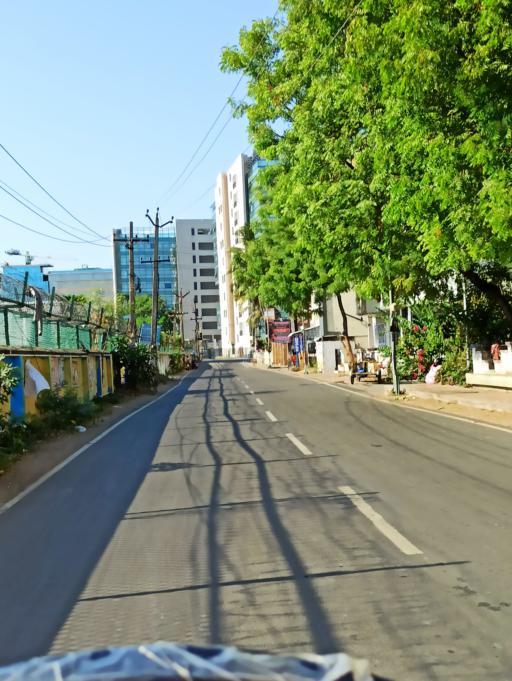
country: IN
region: Tamil Nadu
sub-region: Thiruvallur
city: Porur
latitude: 13.0281
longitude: 80.1684
